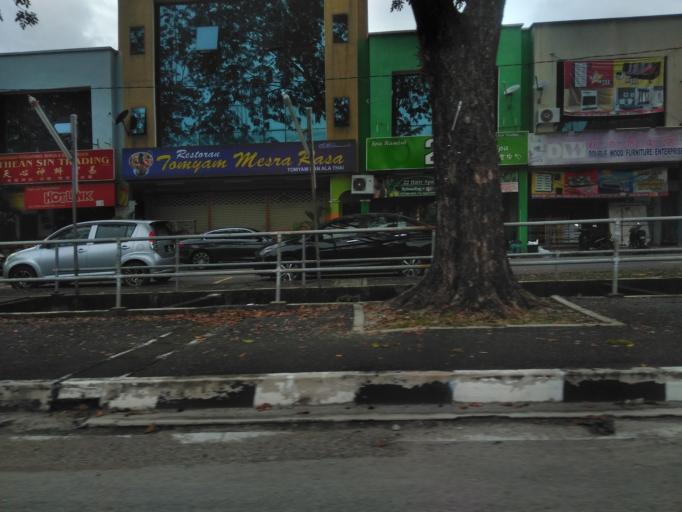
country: MY
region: Penang
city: Bukit Mertajam
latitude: 5.3322
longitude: 100.4850
